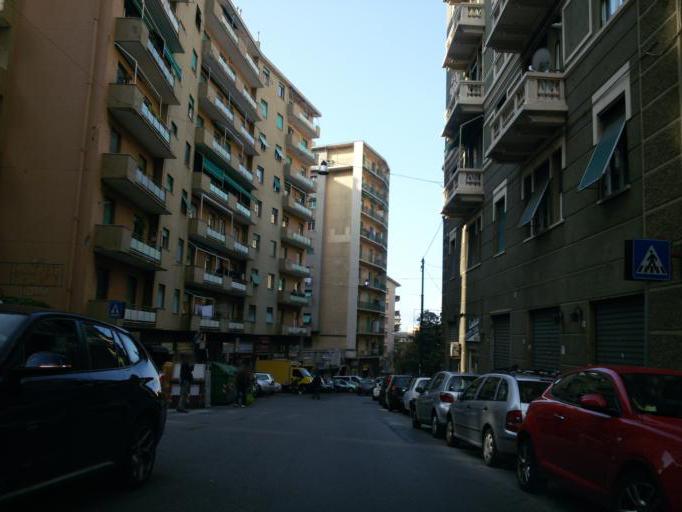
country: IT
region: Liguria
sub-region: Provincia di Genova
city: San Teodoro
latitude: 44.4156
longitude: 8.8951
